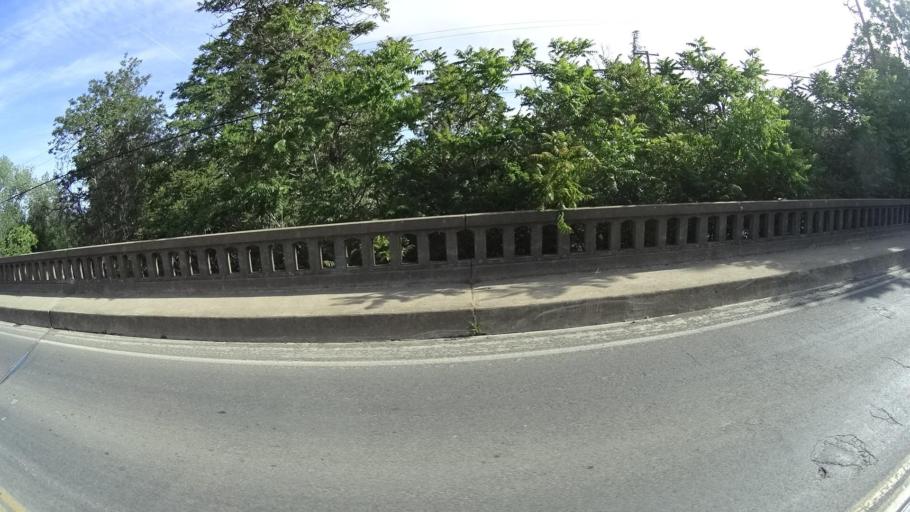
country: US
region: California
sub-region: Lake County
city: Kelseyville
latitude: 38.9784
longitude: -122.8424
